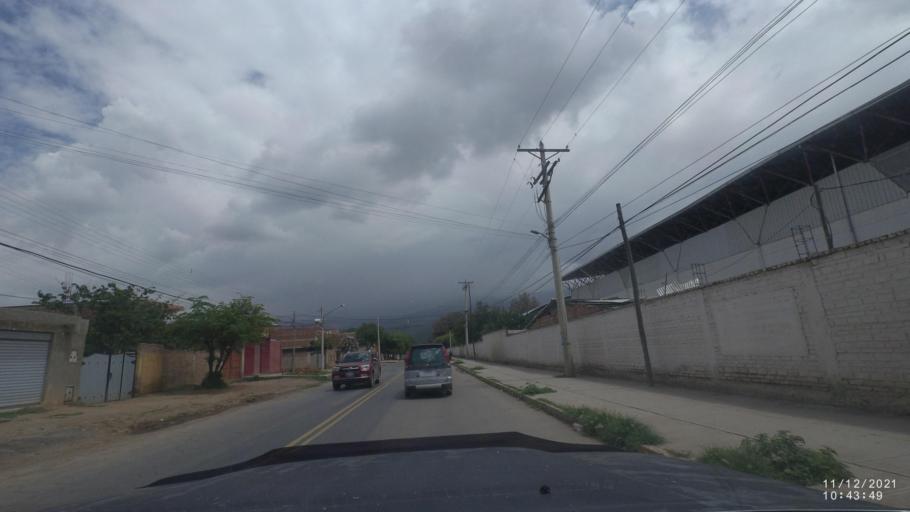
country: BO
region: Cochabamba
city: Cochabamba
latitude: -17.4206
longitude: -66.1312
